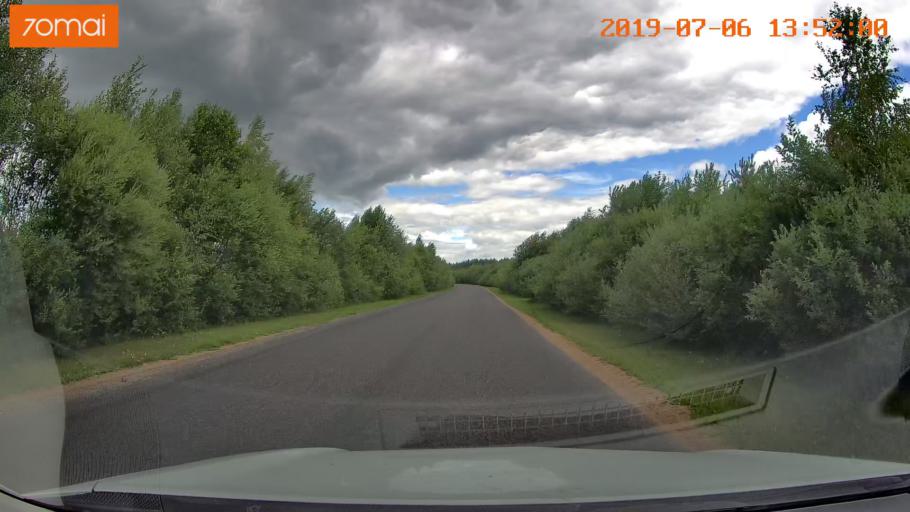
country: BY
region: Minsk
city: Ivyanyets
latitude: 53.7153
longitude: 26.8302
